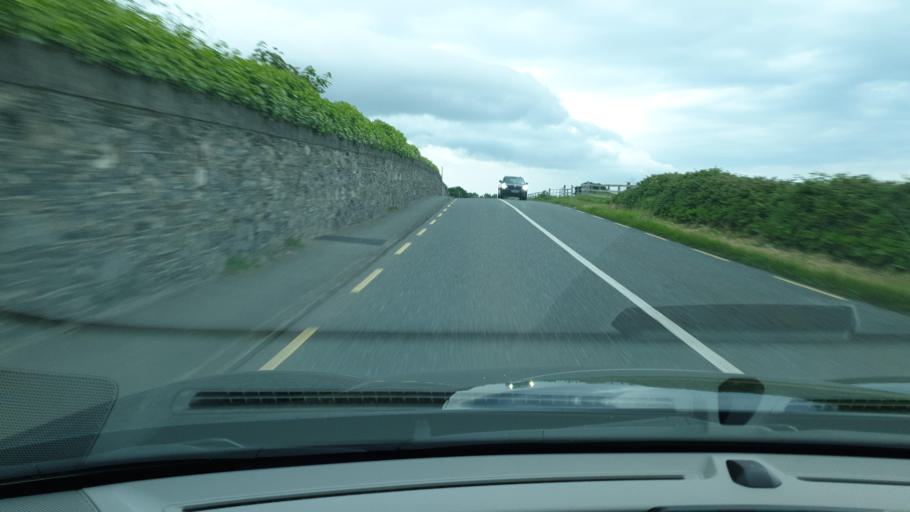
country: IE
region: Leinster
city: Balbriggan
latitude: 53.5992
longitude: -6.1639
